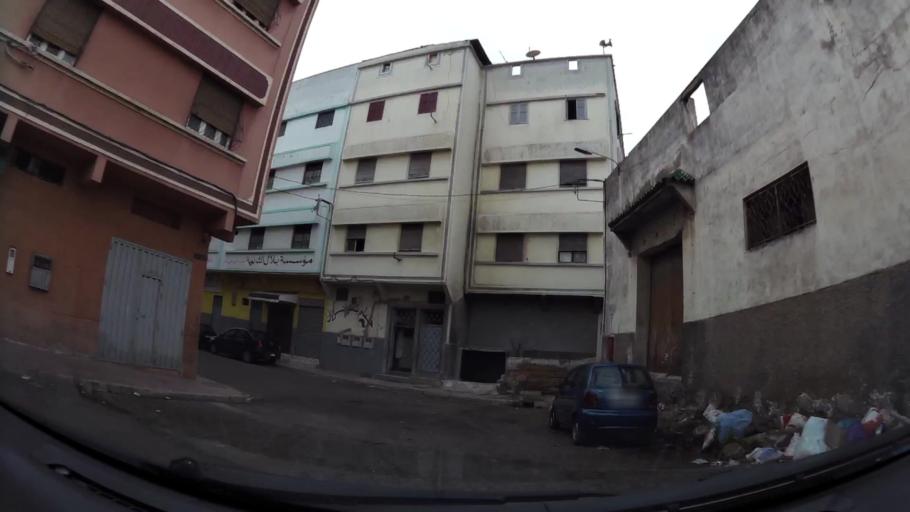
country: MA
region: Grand Casablanca
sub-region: Casablanca
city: Casablanca
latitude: 33.5582
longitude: -7.5970
